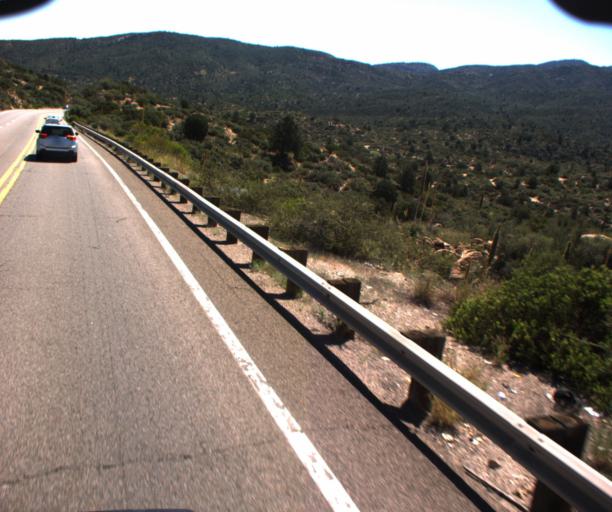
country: US
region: Arizona
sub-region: Gila County
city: Miami
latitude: 33.3693
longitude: -110.9274
